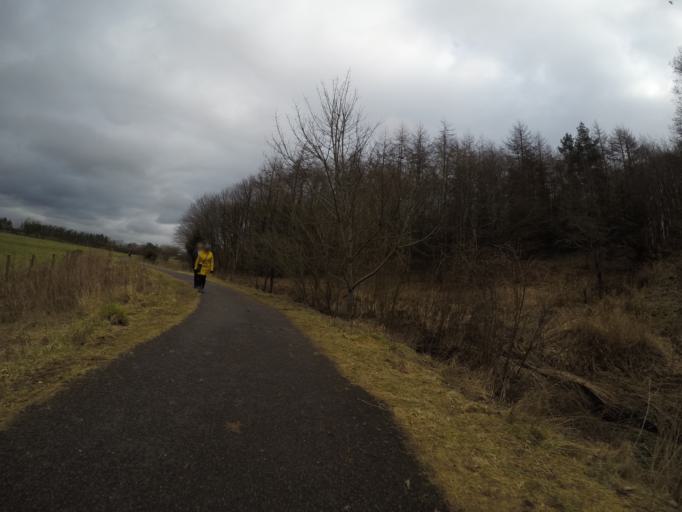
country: GB
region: Scotland
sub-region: North Ayrshire
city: Springside
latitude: 55.6128
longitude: -4.6092
